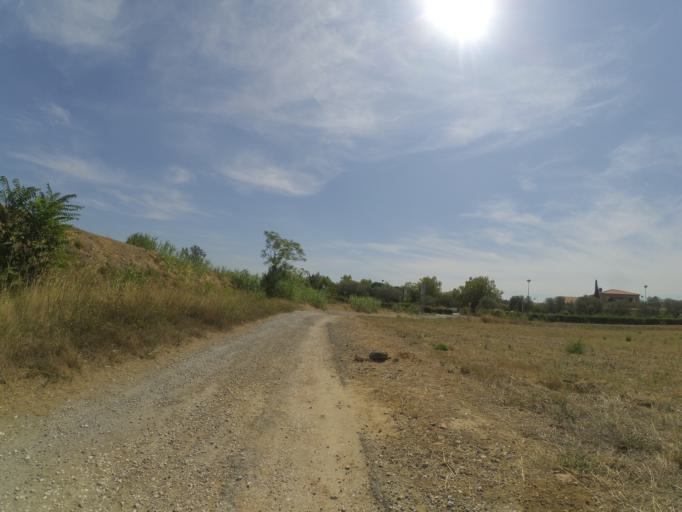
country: FR
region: Languedoc-Roussillon
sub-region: Departement des Pyrenees-Orientales
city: Peyrestortes
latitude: 42.7562
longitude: 2.8577
